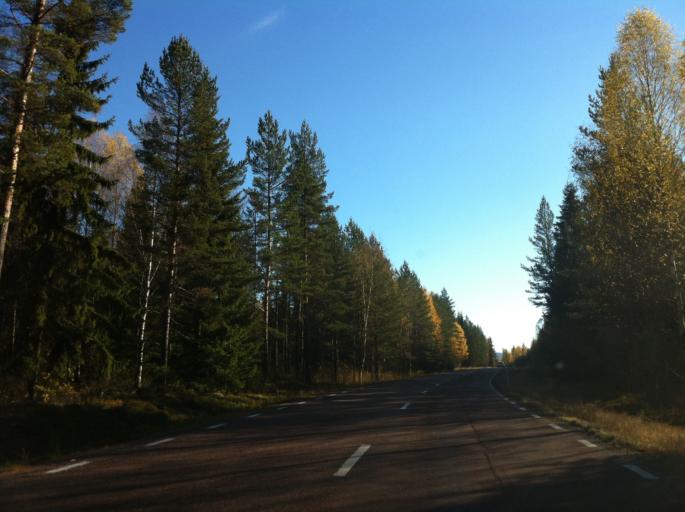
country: SE
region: Dalarna
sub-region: Alvdalens Kommun
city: AElvdalen
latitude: 61.1740
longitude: 14.1023
